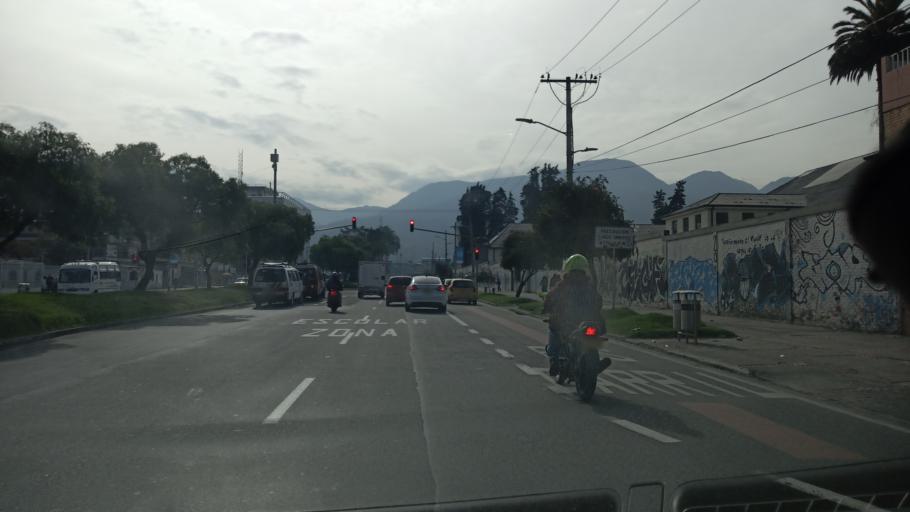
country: CO
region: Bogota D.C.
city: Bogota
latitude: 4.5775
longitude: -74.0971
